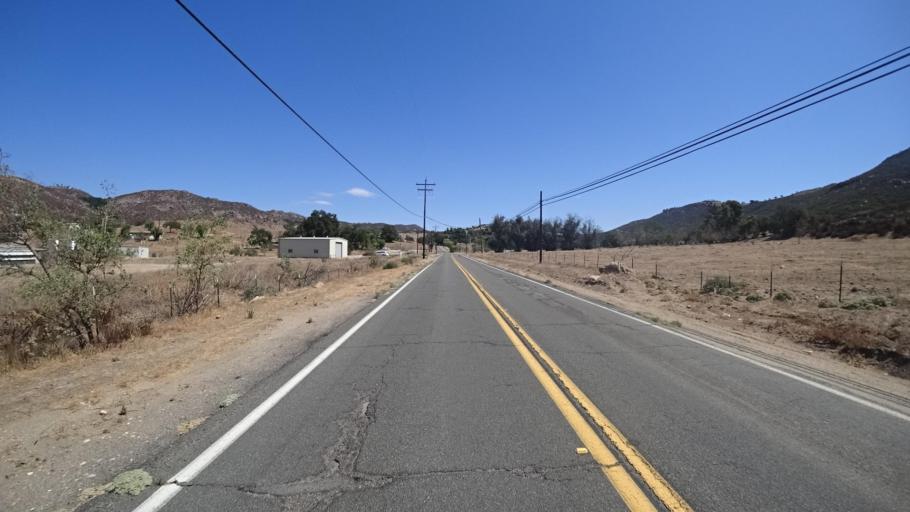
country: US
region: California
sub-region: San Diego County
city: San Diego Country Estates
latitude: 33.0498
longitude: -116.8013
